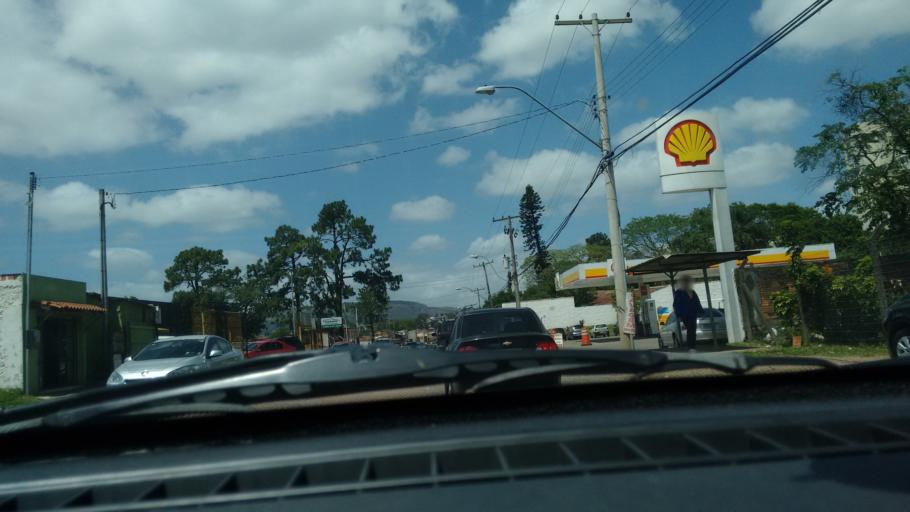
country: BR
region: Rio Grande do Sul
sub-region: Cachoeirinha
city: Cachoeirinha
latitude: -30.0059
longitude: -51.1277
